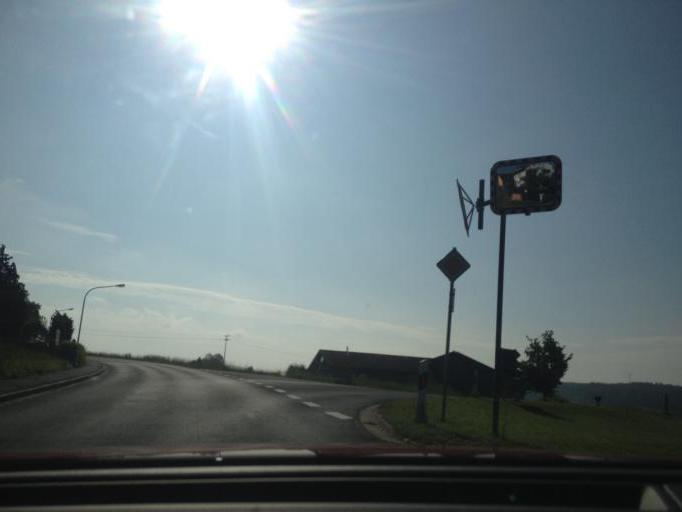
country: DE
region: Bavaria
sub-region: Upper Franconia
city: Pegnitz
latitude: 49.7650
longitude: 11.6073
